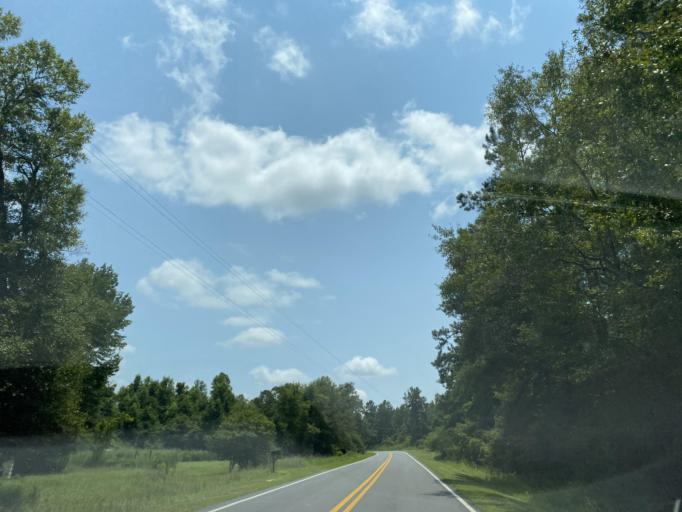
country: US
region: Georgia
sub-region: Telfair County
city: Lumber City
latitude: 31.9457
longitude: -82.6905
